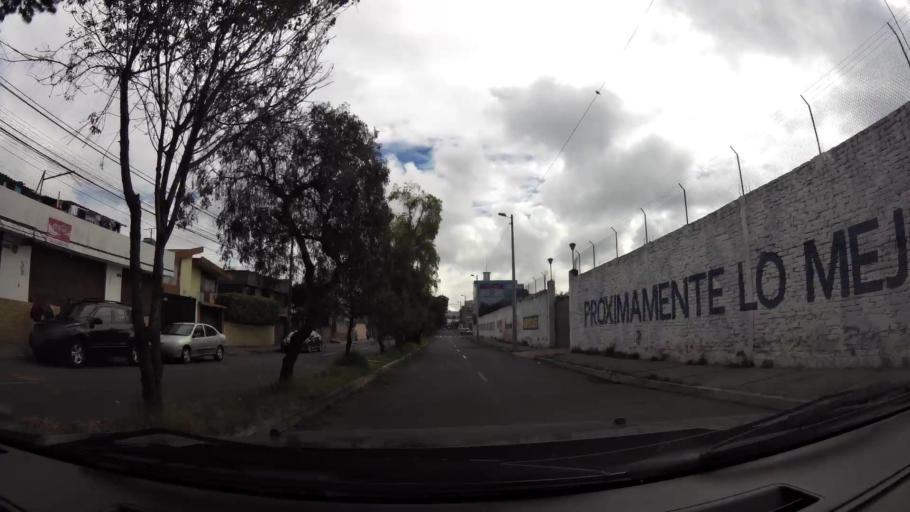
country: EC
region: Pichincha
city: Quito
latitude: -0.1666
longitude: -78.4770
